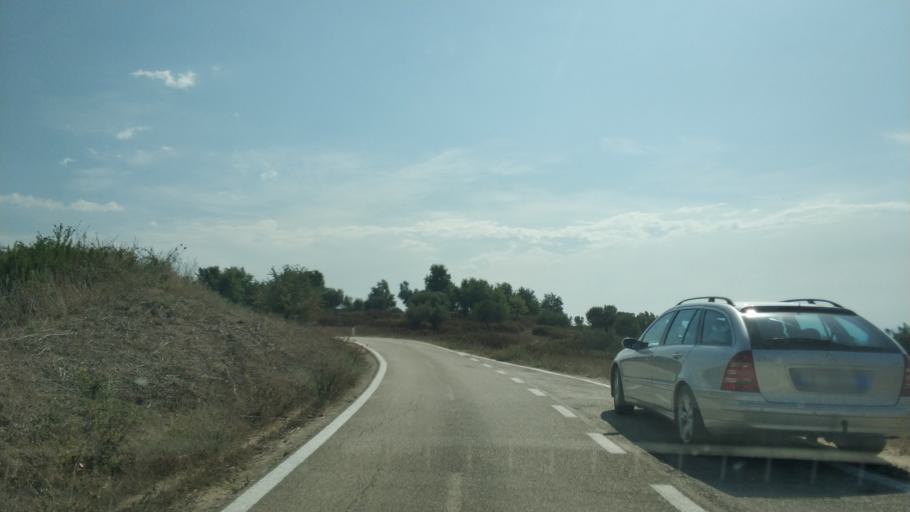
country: AL
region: Fier
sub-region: Rrethi i Fierit
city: Dermenas
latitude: 40.7236
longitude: 19.4691
